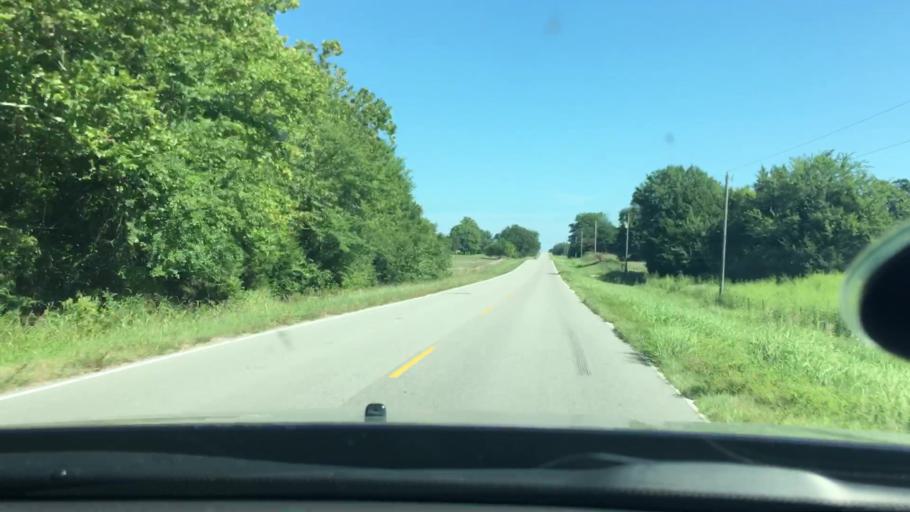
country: US
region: Oklahoma
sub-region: Johnston County
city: Tishomingo
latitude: 34.2896
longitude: -96.5487
